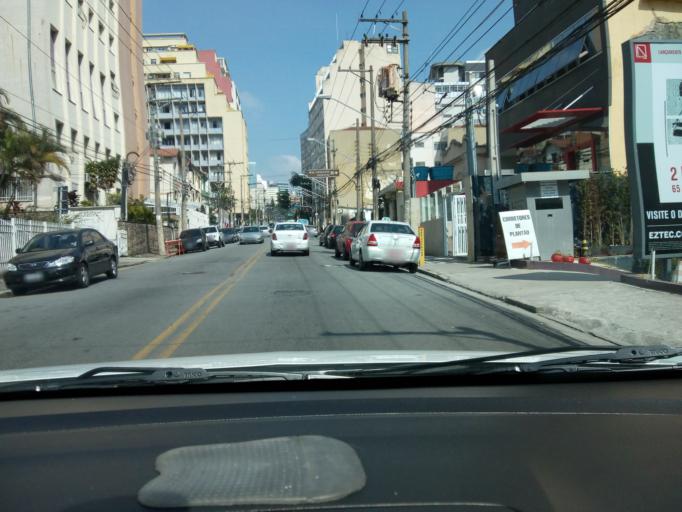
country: BR
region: Sao Paulo
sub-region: Sao Paulo
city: Sao Paulo
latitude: -23.5623
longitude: -46.6335
